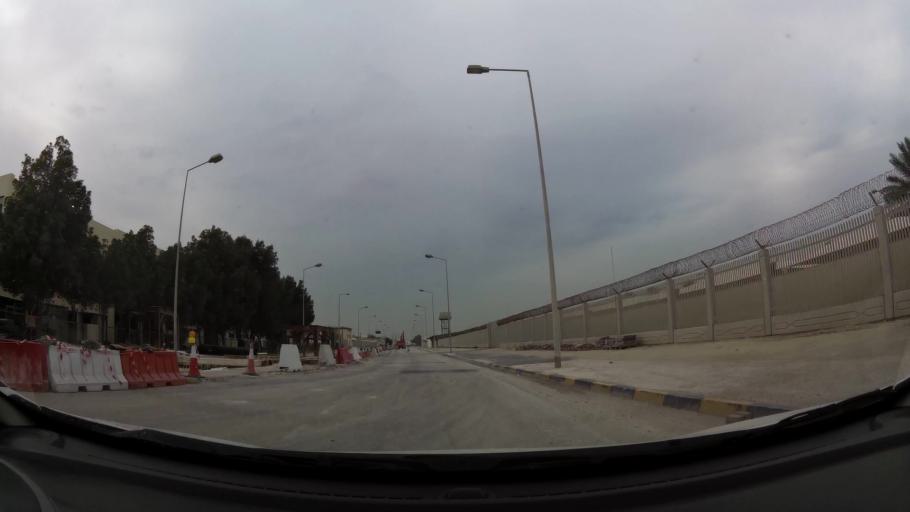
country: BH
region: Northern
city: Sitrah
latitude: 26.1815
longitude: 50.6225
